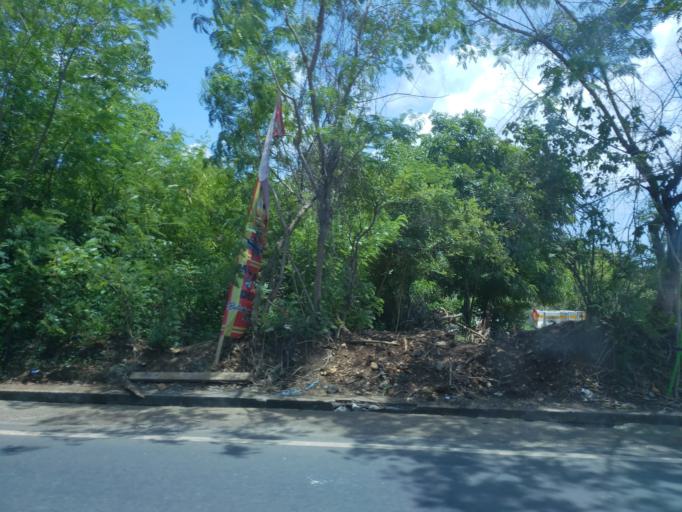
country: ID
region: Bali
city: Jimbaran
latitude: -8.7901
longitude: 115.1640
